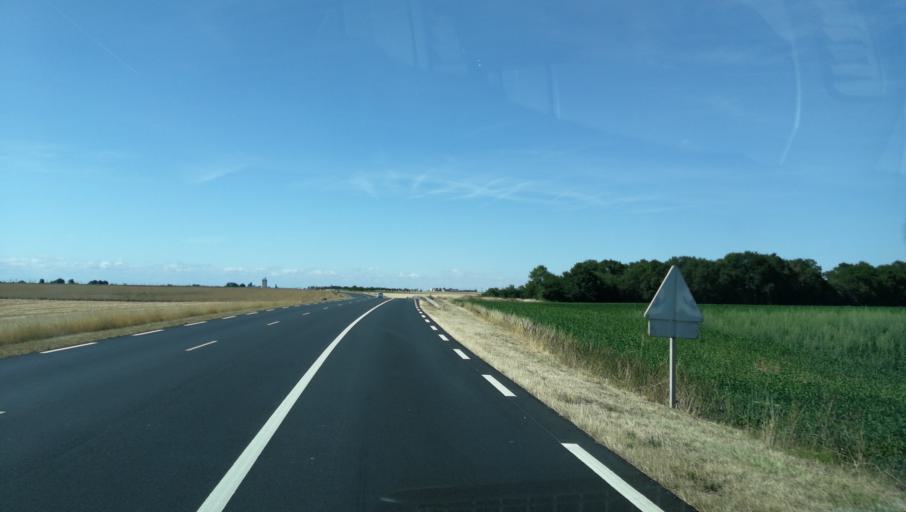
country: FR
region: Ile-de-France
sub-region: Departement de l'Essonne
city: Angerville
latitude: 48.2867
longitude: 1.9800
